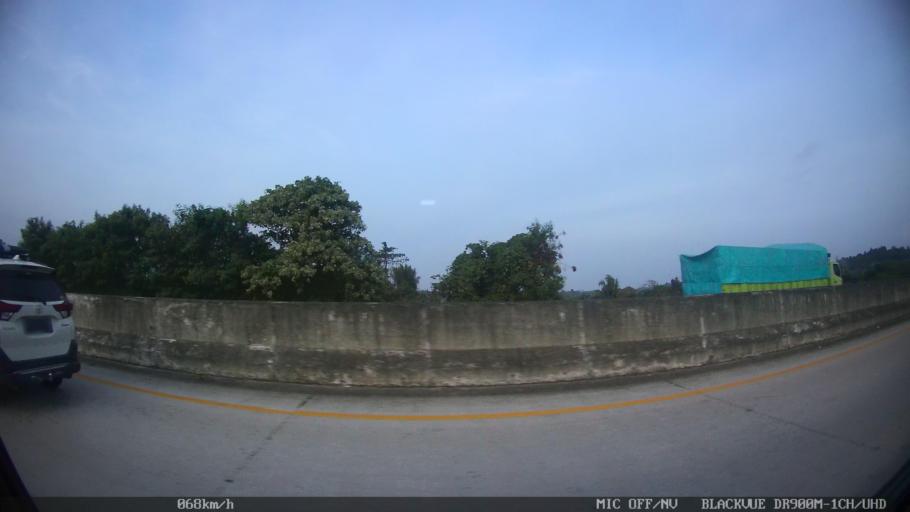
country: ID
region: Lampung
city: Penengahan
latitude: -5.7692
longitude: 105.7157
